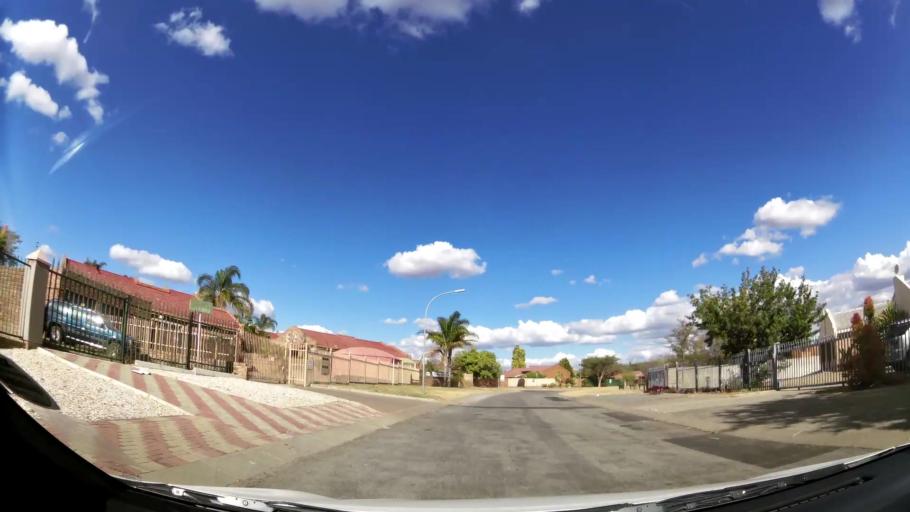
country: ZA
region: Limpopo
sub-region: Capricorn District Municipality
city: Polokwane
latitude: -23.8868
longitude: 29.4712
